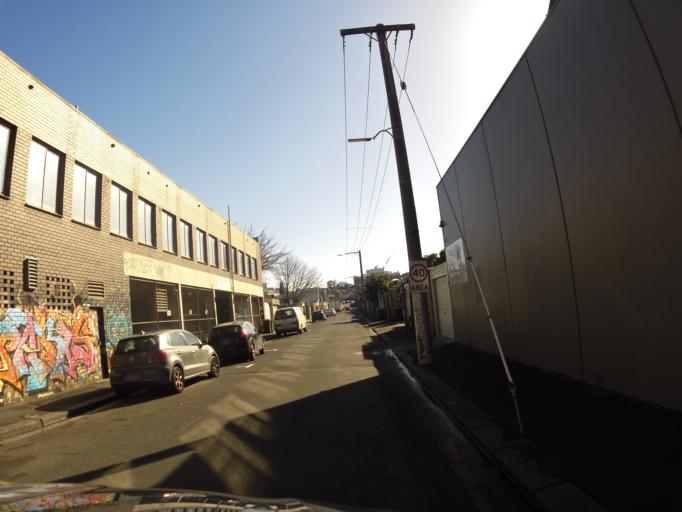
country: AU
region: Victoria
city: Albert Park
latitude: -37.8251
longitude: 144.9940
